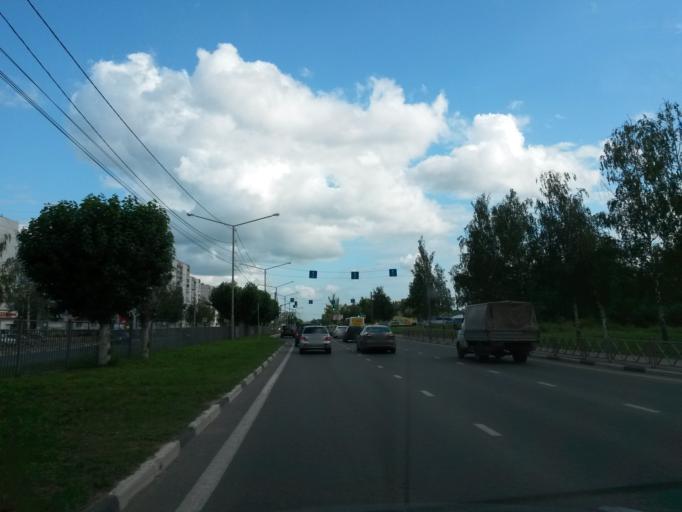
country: RU
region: Jaroslavl
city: Yaroslavl
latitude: 57.5817
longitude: 39.9105
